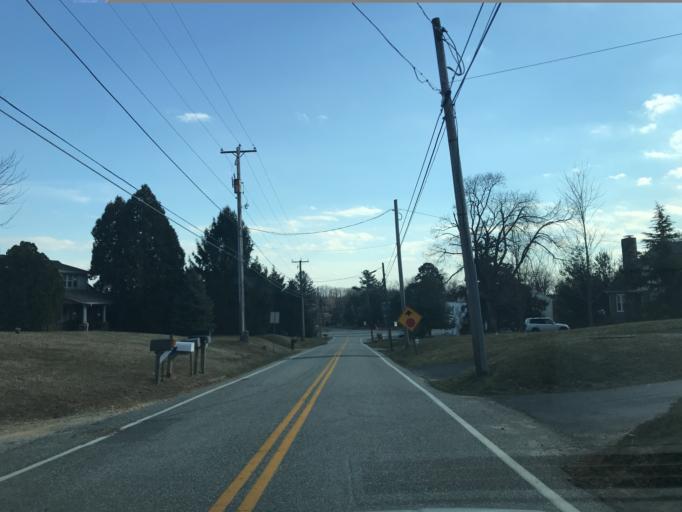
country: US
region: Maryland
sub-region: Cecil County
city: North East
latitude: 39.6434
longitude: -75.9615
